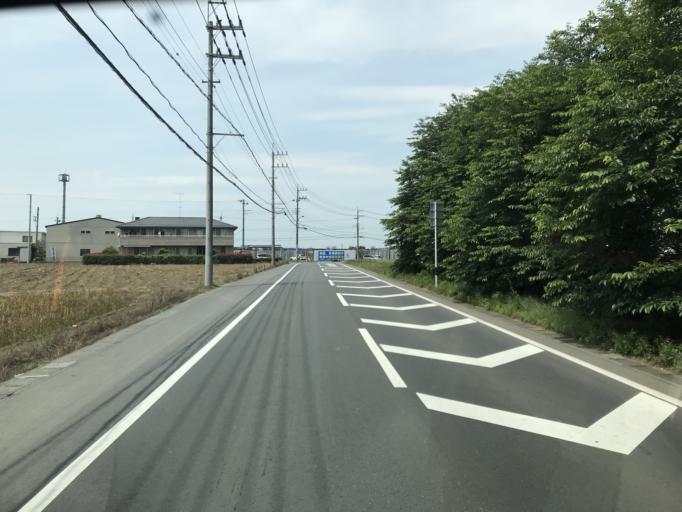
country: JP
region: Ibaraki
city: Iwai
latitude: 36.0337
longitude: 139.8337
